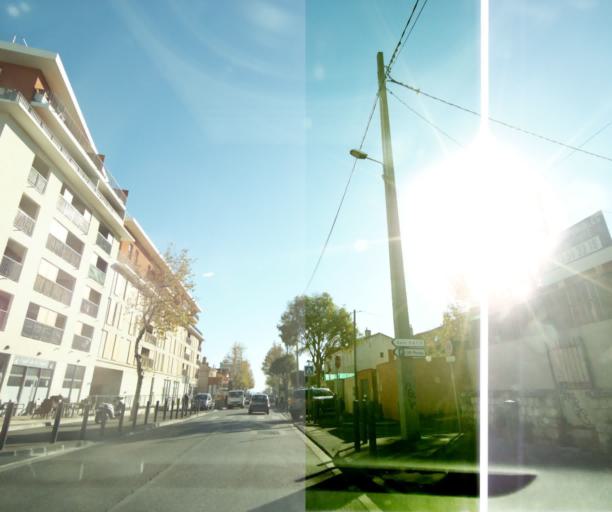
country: FR
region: Provence-Alpes-Cote d'Azur
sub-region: Departement des Bouches-du-Rhone
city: Marseille 15
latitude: 43.3692
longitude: 5.3564
